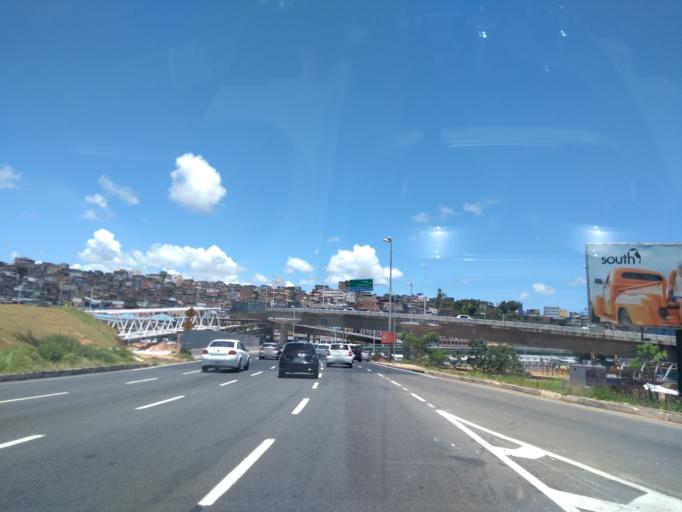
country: BR
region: Bahia
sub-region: Salvador
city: Salvador
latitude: -12.9771
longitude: -38.4609
